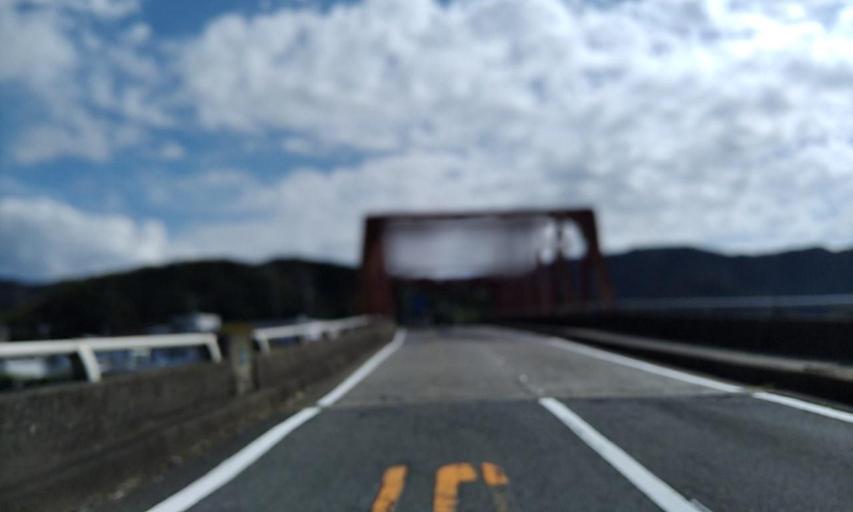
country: JP
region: Wakayama
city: Gobo
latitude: 33.9603
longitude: 135.1145
